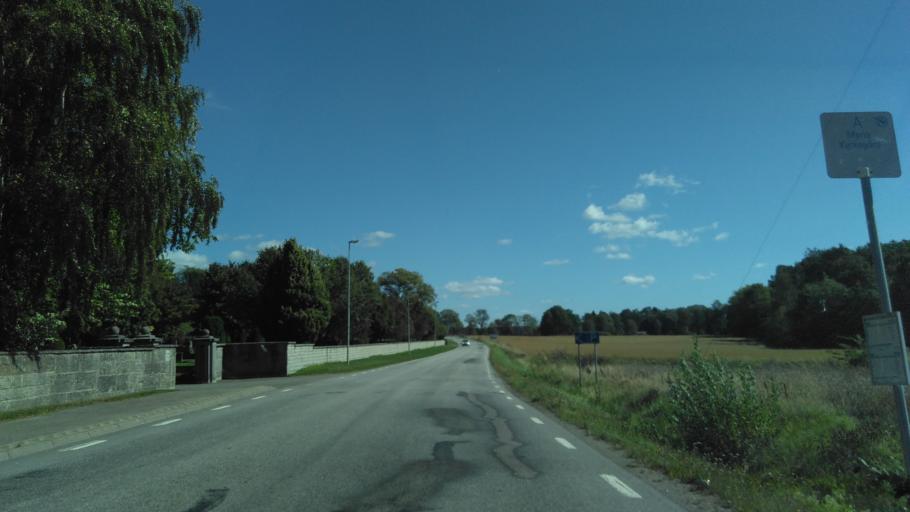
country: SE
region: Vaestra Goetaland
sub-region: Skara Kommun
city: Skara
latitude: 58.3841
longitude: 13.4650
